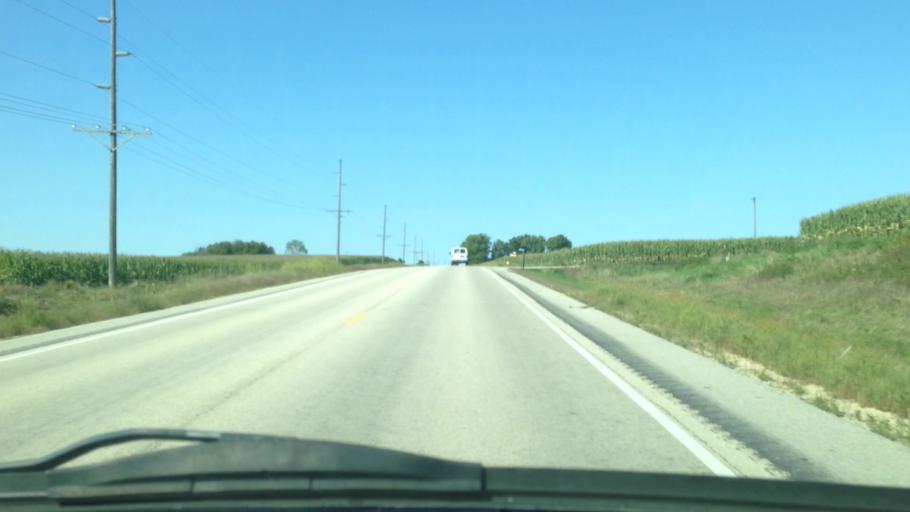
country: US
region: Minnesota
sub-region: Fillmore County
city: Rushford
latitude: 43.9146
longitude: -91.7401
